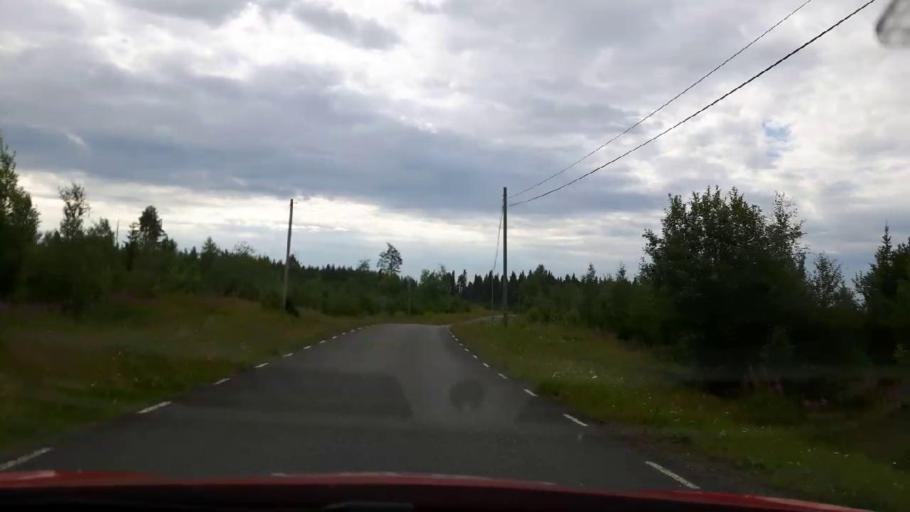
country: SE
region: Jaemtland
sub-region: OEstersunds Kommun
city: Lit
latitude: 63.3933
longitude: 15.0099
